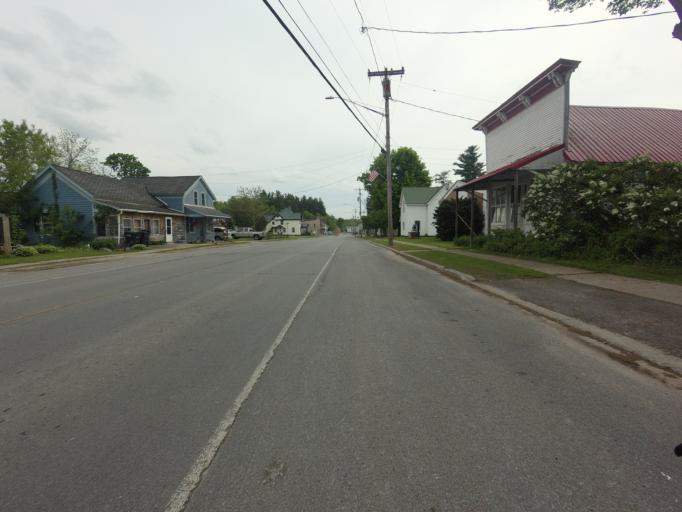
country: US
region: New York
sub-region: St. Lawrence County
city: Gouverneur
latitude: 44.3262
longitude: -75.2500
